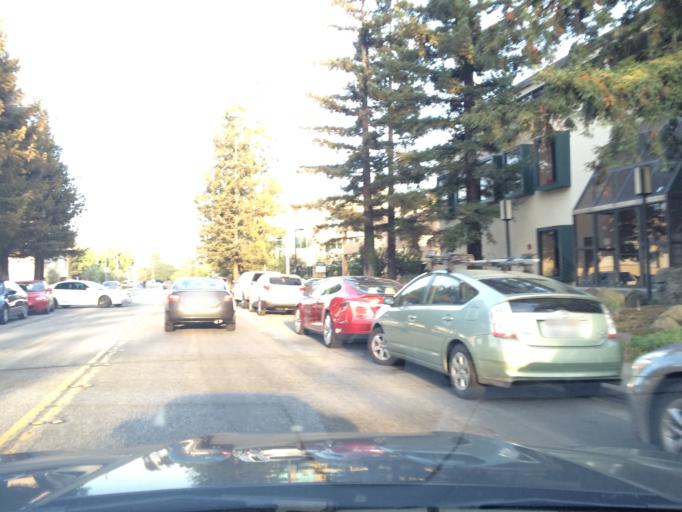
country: US
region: California
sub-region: Santa Clara County
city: Cupertino
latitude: 37.3302
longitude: -122.0343
